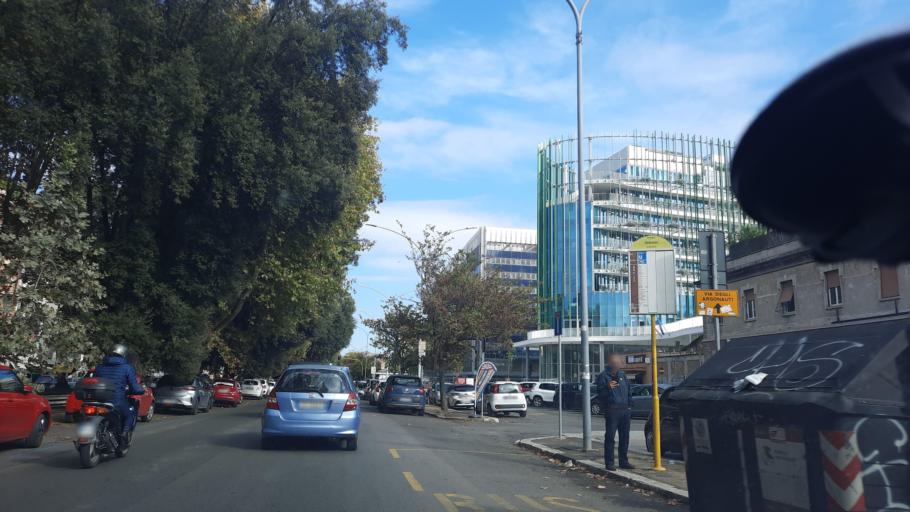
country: IT
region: Latium
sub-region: Citta metropolitana di Roma Capitale
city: Rome
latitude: 41.8640
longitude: 12.4791
